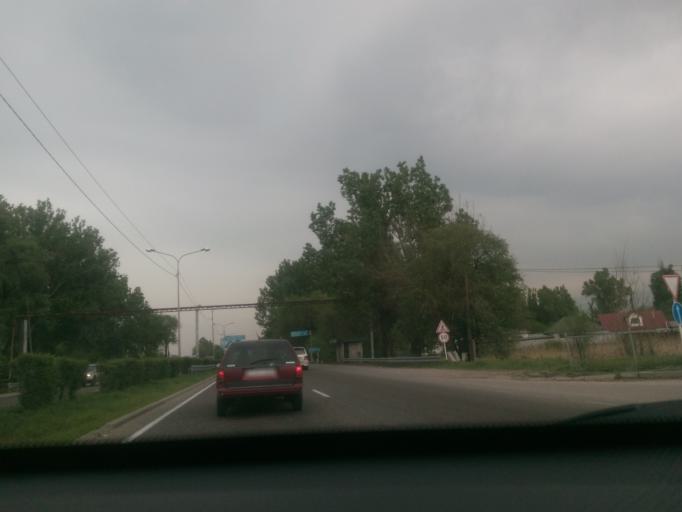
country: KZ
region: Almaty Oblysy
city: Burunday
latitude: 43.2267
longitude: 76.7415
